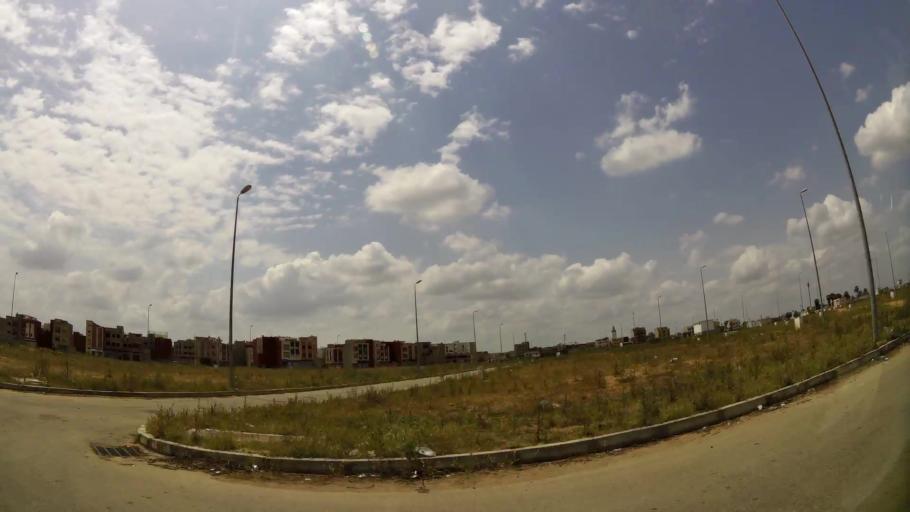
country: MA
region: Rabat-Sale-Zemmour-Zaer
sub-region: Khemisset
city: Tiflet
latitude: 34.0139
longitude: -6.5285
